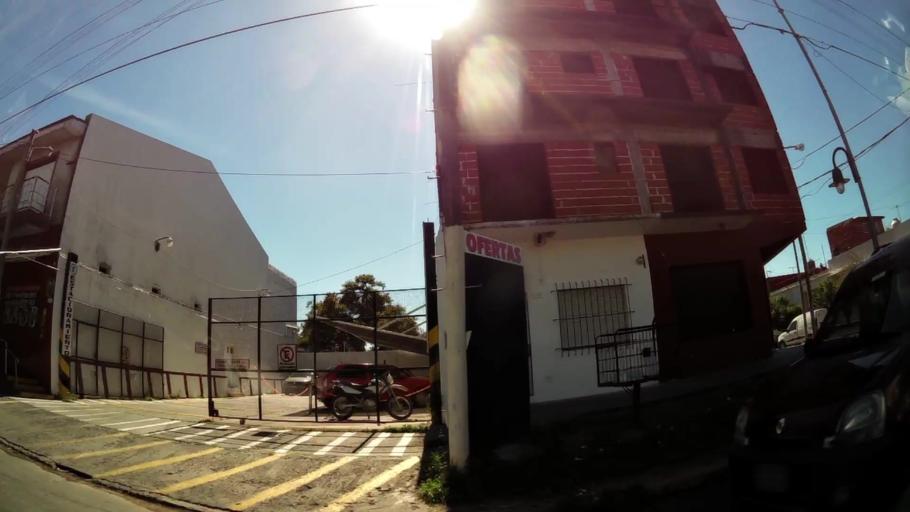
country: AR
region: Buenos Aires
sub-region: Partido de Tigre
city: Tigre
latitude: -34.4943
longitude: -58.6118
